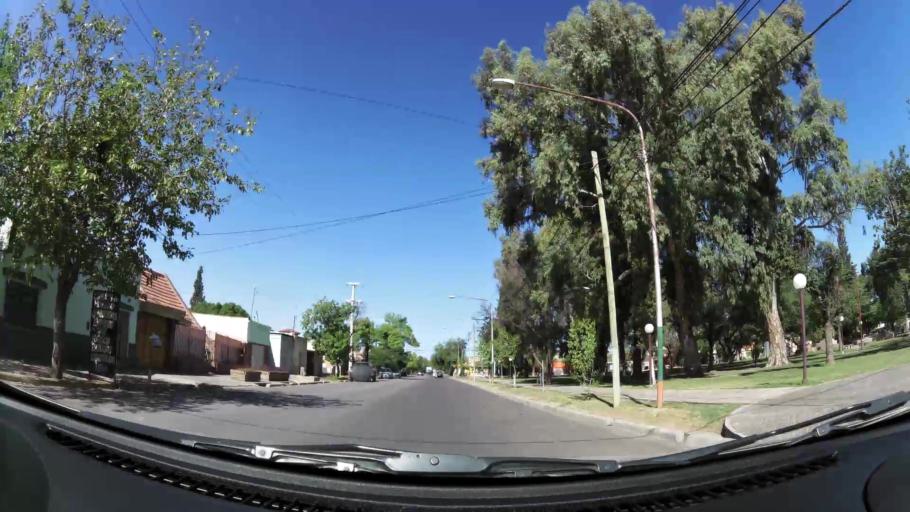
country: AR
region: Mendoza
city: Mendoza
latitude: -32.8930
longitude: -68.8093
